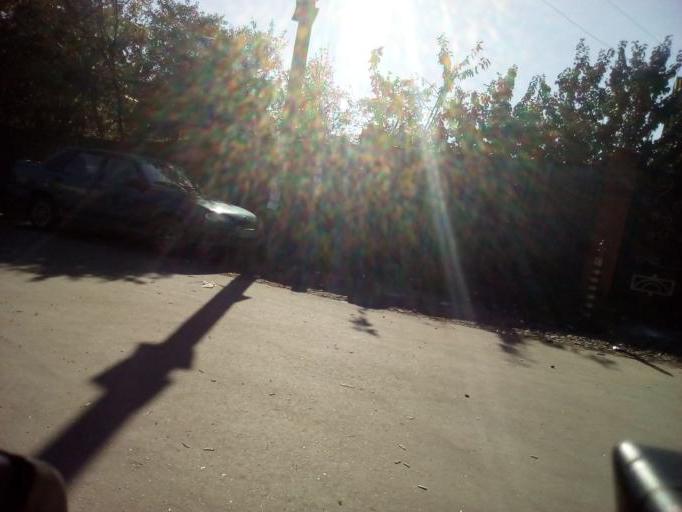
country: RU
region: Moskovskaya
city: Ramenskoye
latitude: 55.5596
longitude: 38.2408
